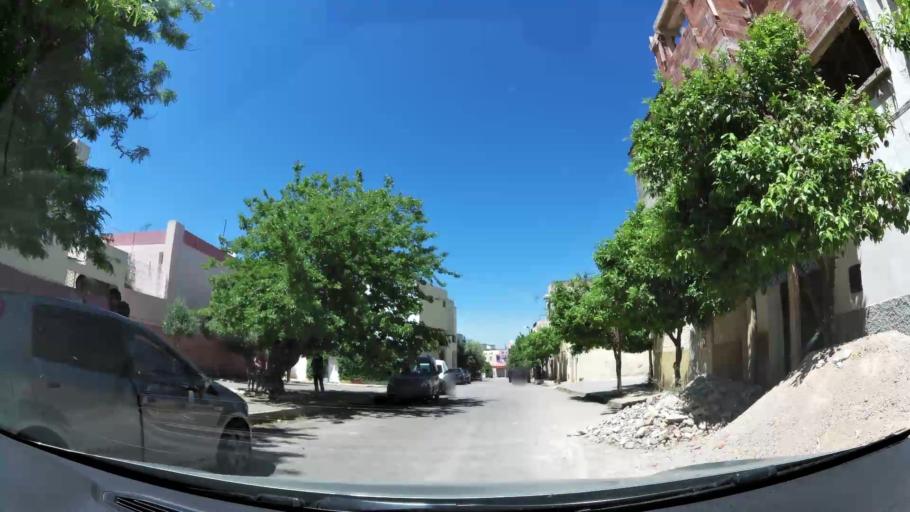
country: MA
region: Fes-Boulemane
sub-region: Fes
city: Fes
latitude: 34.0228
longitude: -5.0042
